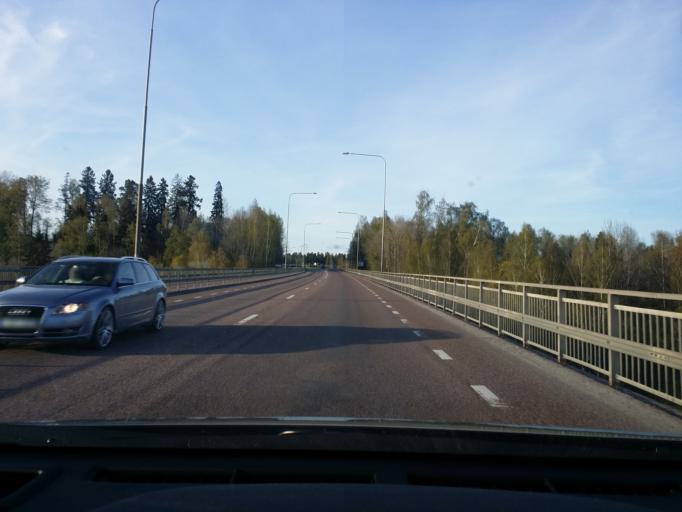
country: SE
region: Dalarna
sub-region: Avesta Kommun
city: Avesta
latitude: 60.1477
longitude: 16.1996
